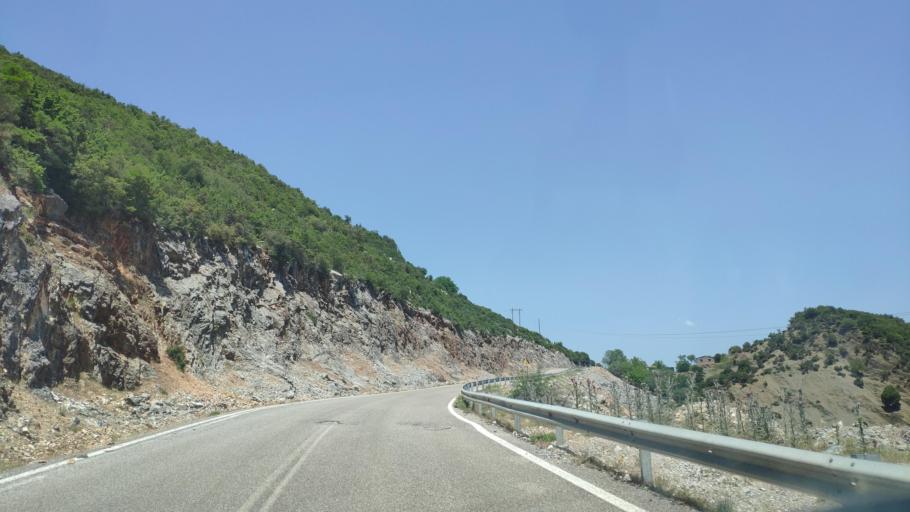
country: GR
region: Central Greece
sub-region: Nomos Evrytanias
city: Kerasochori
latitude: 39.1018
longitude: 21.4105
